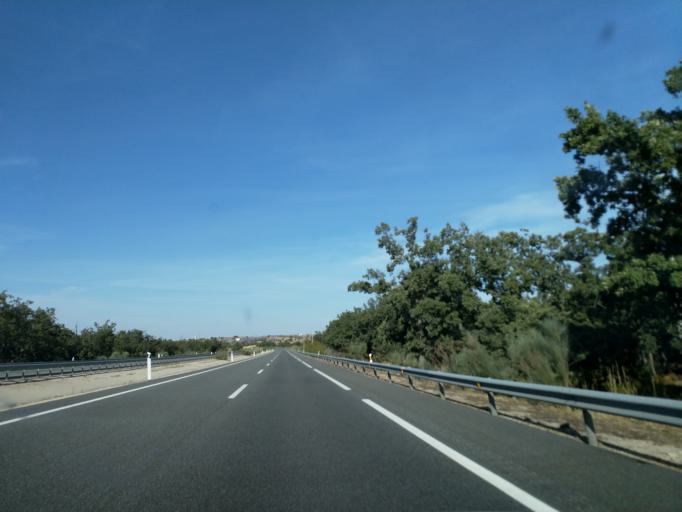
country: ES
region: Castille and Leon
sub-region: Provincia de Segovia
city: Villacastin
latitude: 40.7557
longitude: -4.4493
